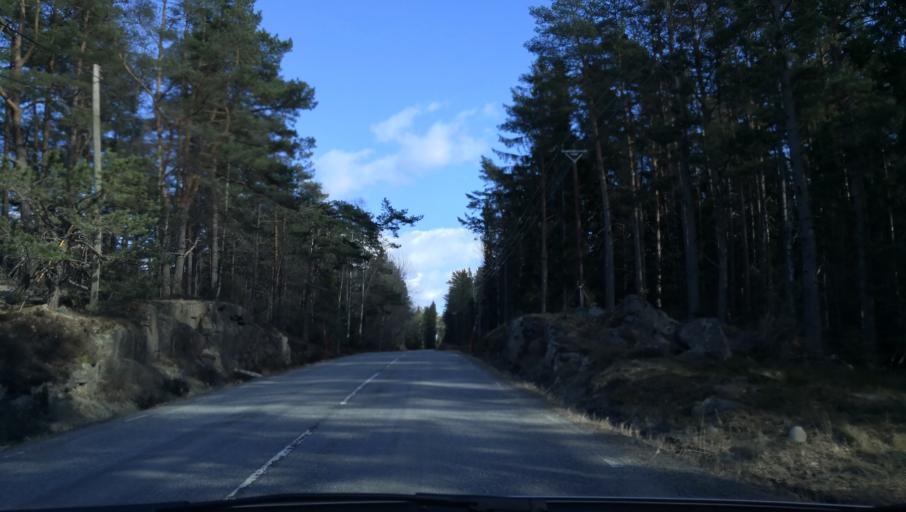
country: SE
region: Stockholm
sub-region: Varmdo Kommun
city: Hemmesta
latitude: 59.3570
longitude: 18.5623
